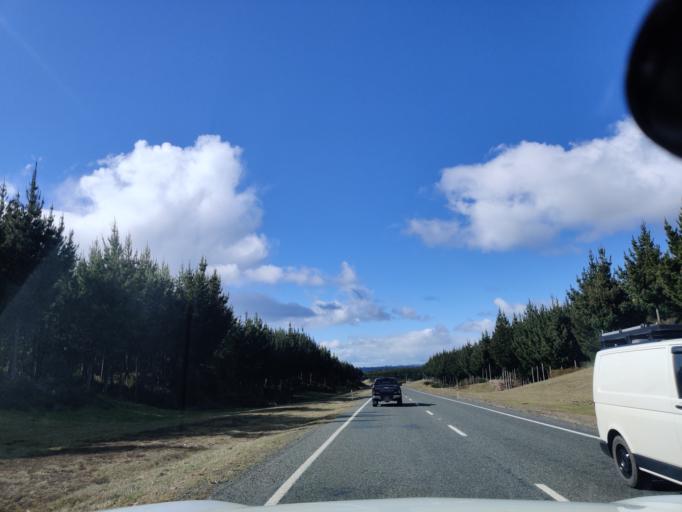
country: NZ
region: Waikato
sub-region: Taupo District
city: Taupo
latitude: -38.8242
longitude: 176.0704
